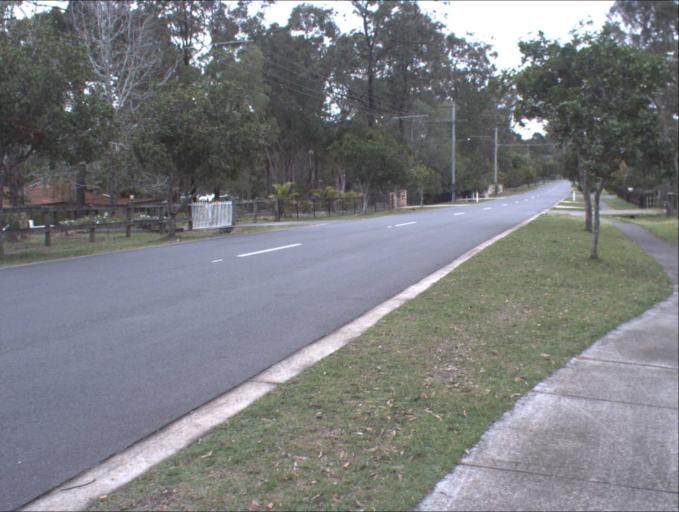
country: AU
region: Queensland
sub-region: Brisbane
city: Forest Lake
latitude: -27.6674
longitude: 153.0069
